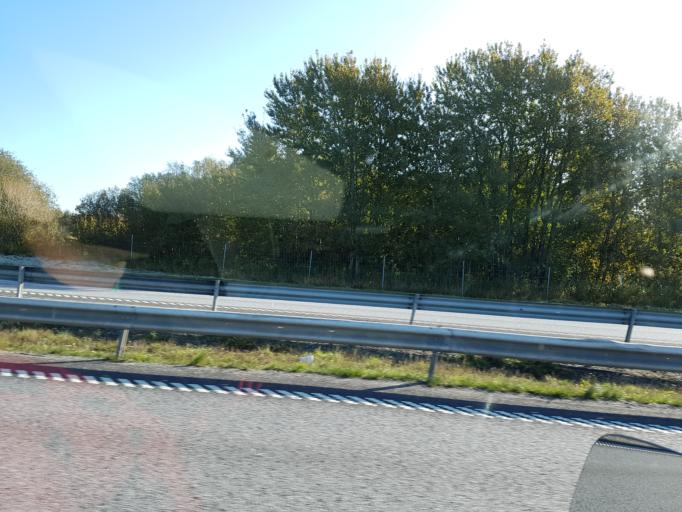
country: SE
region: Vaestra Goetaland
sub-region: Stenungsunds Kommun
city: Stora Hoga
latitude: 58.0166
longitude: 11.8435
